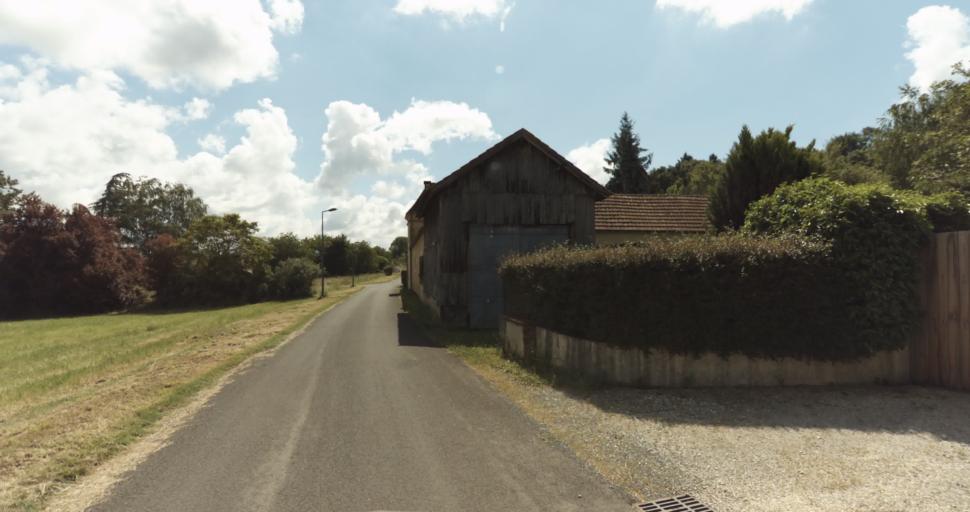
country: FR
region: Aquitaine
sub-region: Departement de la Dordogne
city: Le Bugue
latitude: 44.8411
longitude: 0.9081
